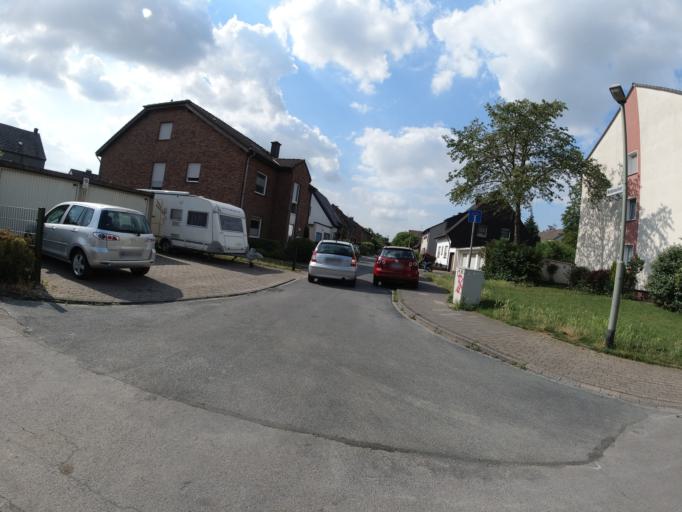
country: DE
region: North Rhine-Westphalia
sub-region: Regierungsbezirk Dusseldorf
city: Moers
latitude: 51.3940
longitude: 6.6739
